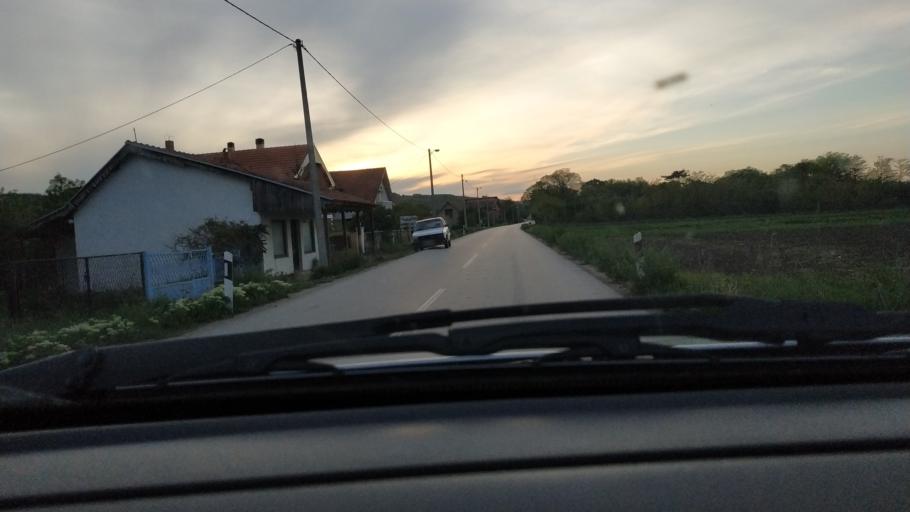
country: RS
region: Central Serbia
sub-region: Nisavski Okrug
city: Aleksinac
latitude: 43.5515
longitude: 21.6168
